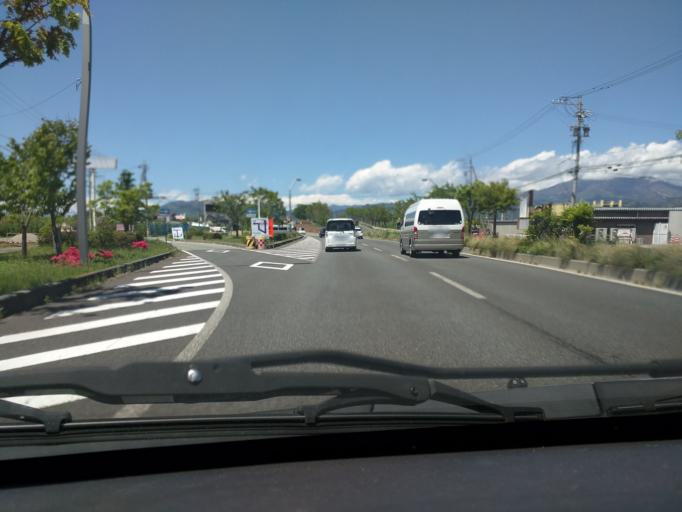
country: JP
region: Nagano
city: Suzaka
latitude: 36.6385
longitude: 138.2677
